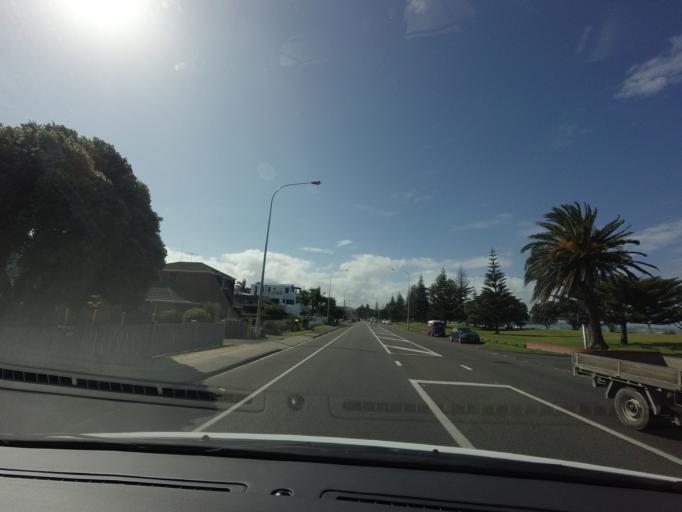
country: NZ
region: Auckland
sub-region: Auckland
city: Rothesay Bay
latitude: -36.5915
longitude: 174.6983
